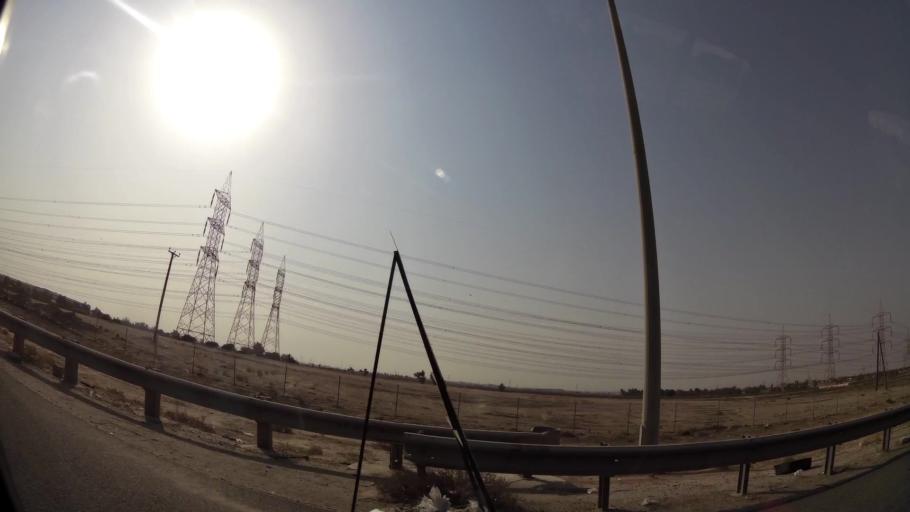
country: KW
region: Muhafazat al Jahra'
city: Al Jahra'
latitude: 29.3042
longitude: 47.7840
